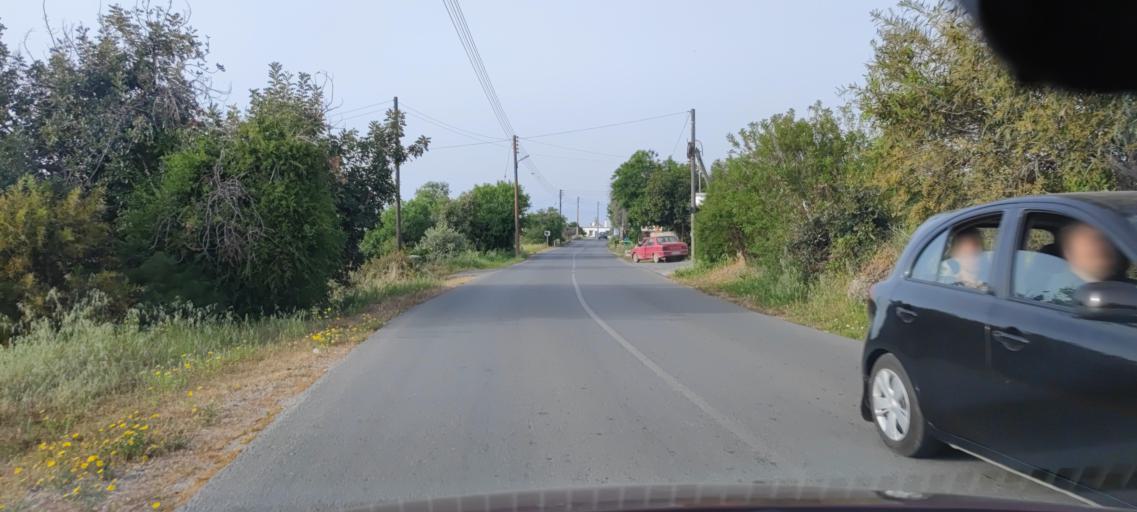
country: CY
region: Ammochostos
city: Leonarisso
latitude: 35.5383
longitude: 34.1933
